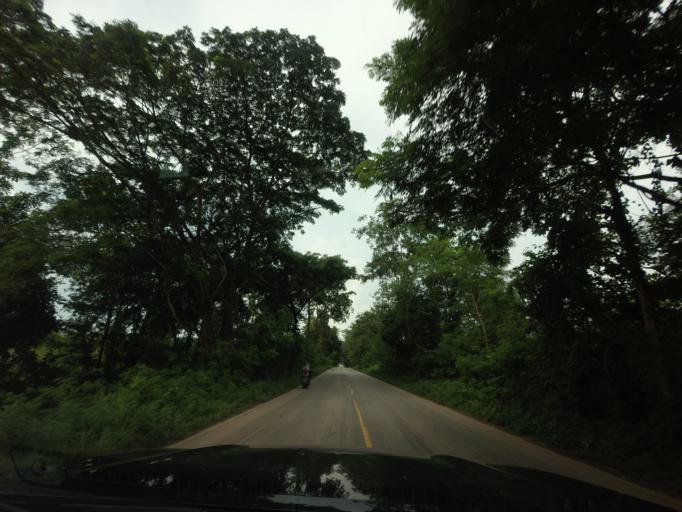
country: TH
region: Changwat Nong Bua Lamphu
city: Suwannakhuha
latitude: 17.4806
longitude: 102.3633
